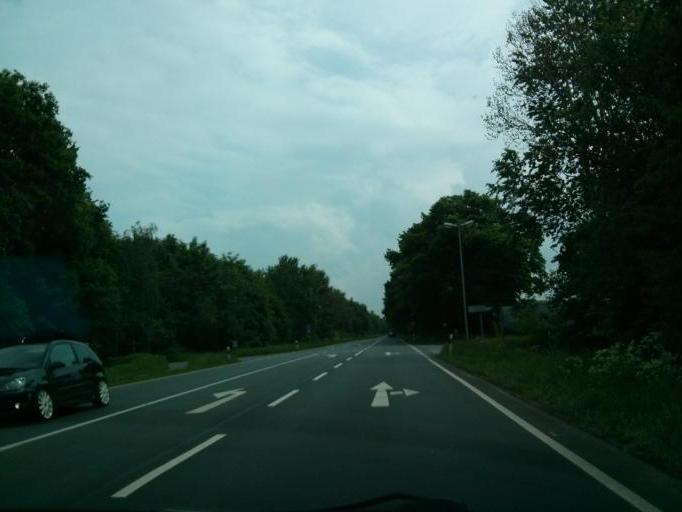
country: DE
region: Lower Saxony
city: Loxstedt
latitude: 53.4870
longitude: 8.6690
